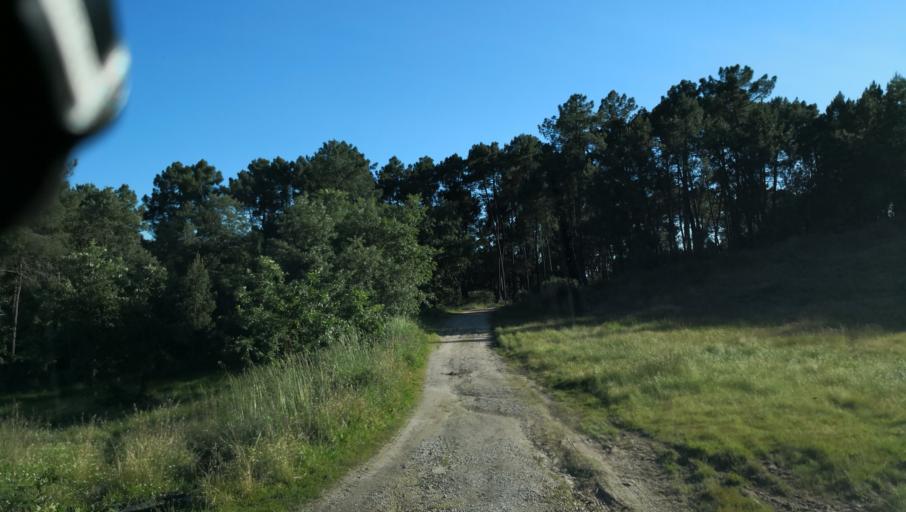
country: PT
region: Vila Real
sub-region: Vila Real
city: Vila Real
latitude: 41.3149
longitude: -7.6746
